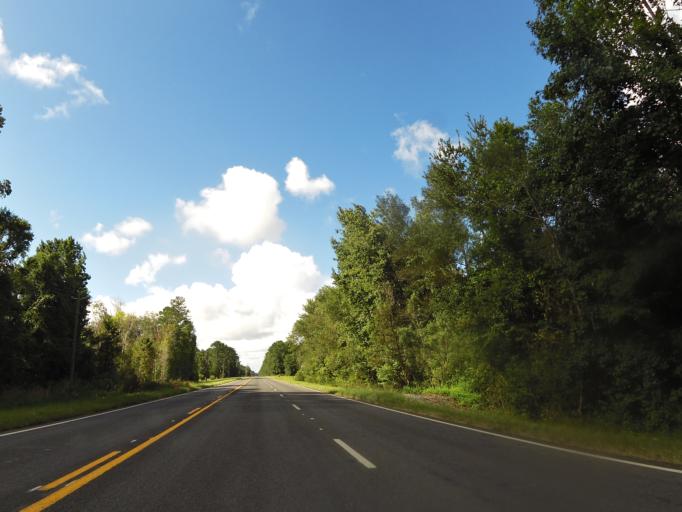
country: US
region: Georgia
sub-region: Camden County
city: Kingsland
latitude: 30.8463
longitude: -81.6995
